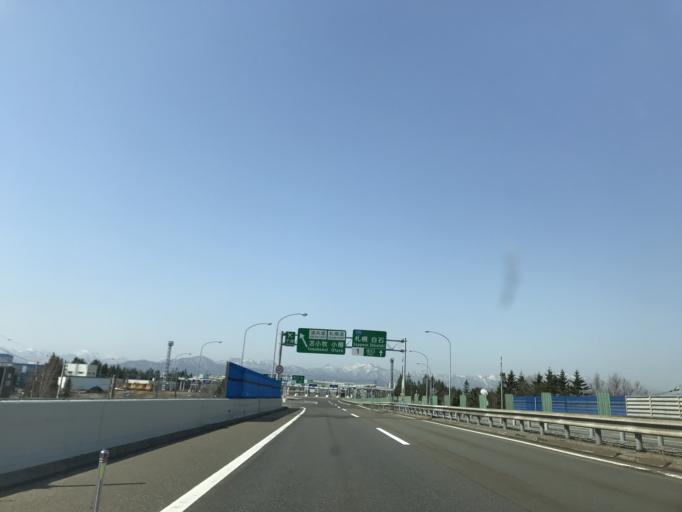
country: JP
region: Hokkaido
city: Sapporo
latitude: 43.0804
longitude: 141.4303
